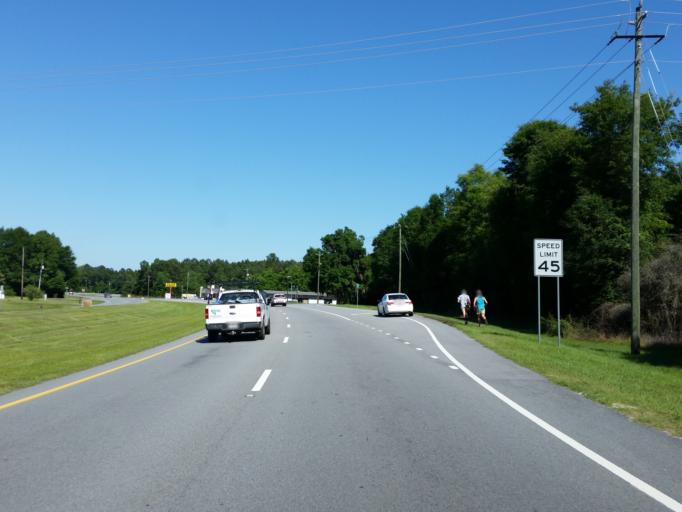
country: US
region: Georgia
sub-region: Lowndes County
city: Valdosta
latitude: 30.6866
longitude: -83.1970
